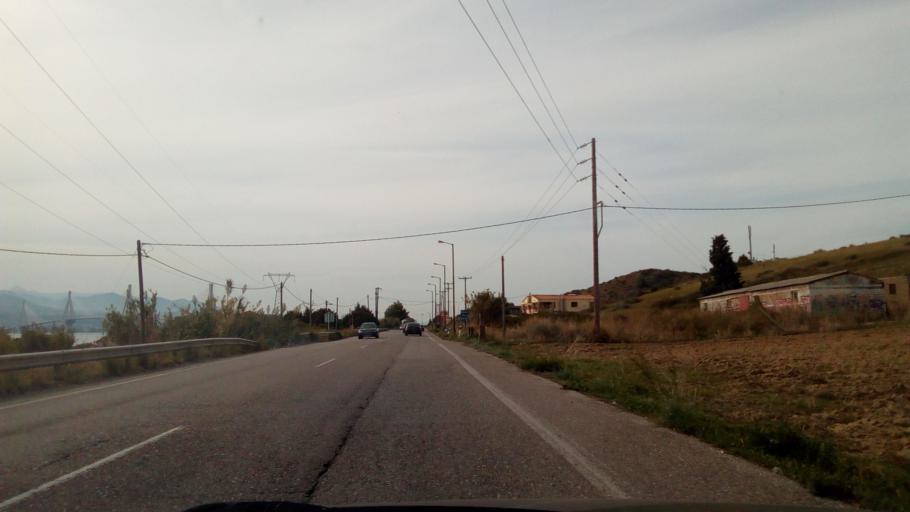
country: GR
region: West Greece
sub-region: Nomos Aitolias kai Akarnanias
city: Antirrio
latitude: 38.3480
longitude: 21.7714
